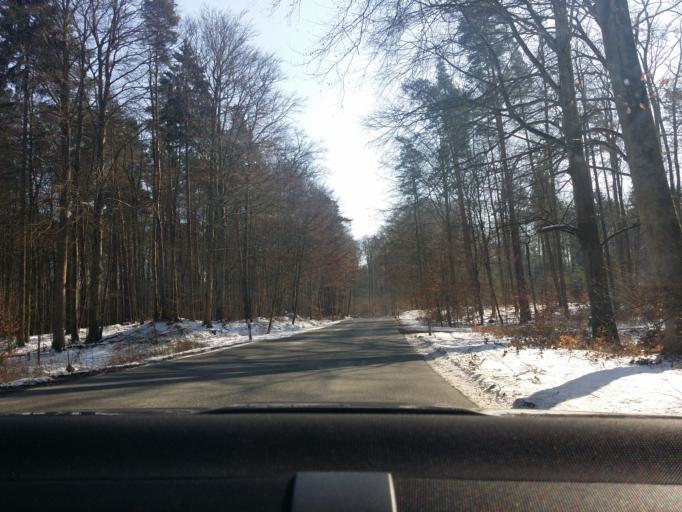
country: DE
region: Mecklenburg-Vorpommern
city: Rechlin
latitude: 53.2399
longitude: 12.6948
